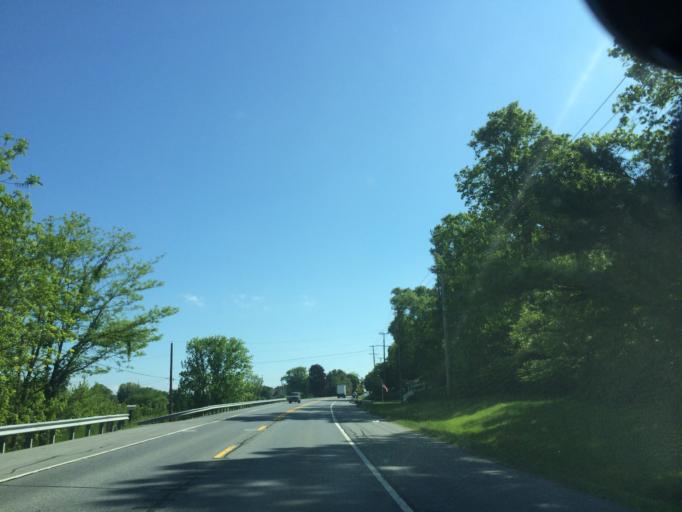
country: US
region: Maryland
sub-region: Carroll County
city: Eldersburg
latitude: 39.4747
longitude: -76.9173
